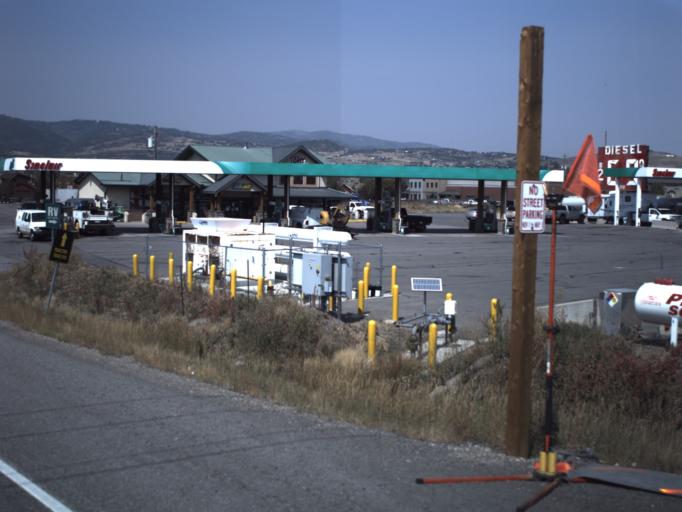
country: US
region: Utah
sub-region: Summit County
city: Snyderville
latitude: 40.7333
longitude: -111.4989
